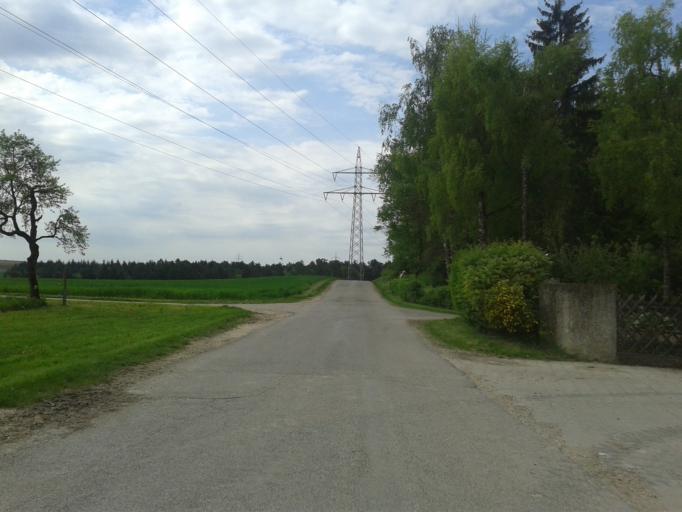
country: DE
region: Baden-Wuerttemberg
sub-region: Tuebingen Region
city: Blaubeuren
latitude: 48.3913
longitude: 9.7887
